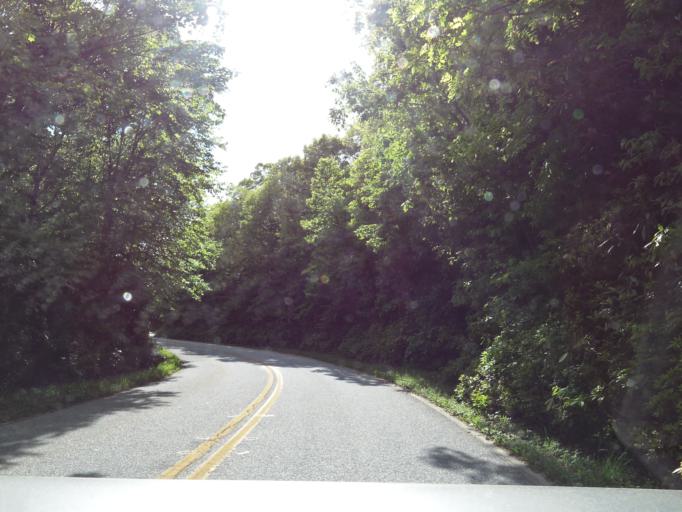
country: US
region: Georgia
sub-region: Towns County
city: Hiawassee
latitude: 34.8699
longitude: -83.8062
